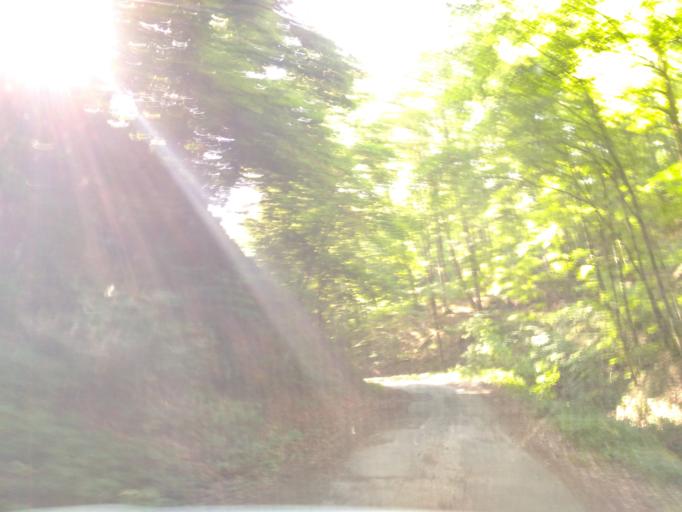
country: HU
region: Baranya
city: Hosszuheteny
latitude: 46.2236
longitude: 18.3321
